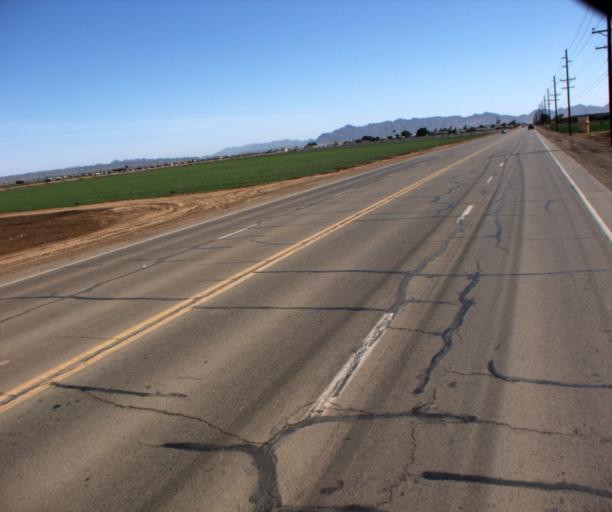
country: US
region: Arizona
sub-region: Yuma County
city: Yuma
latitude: 32.6990
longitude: -114.5402
